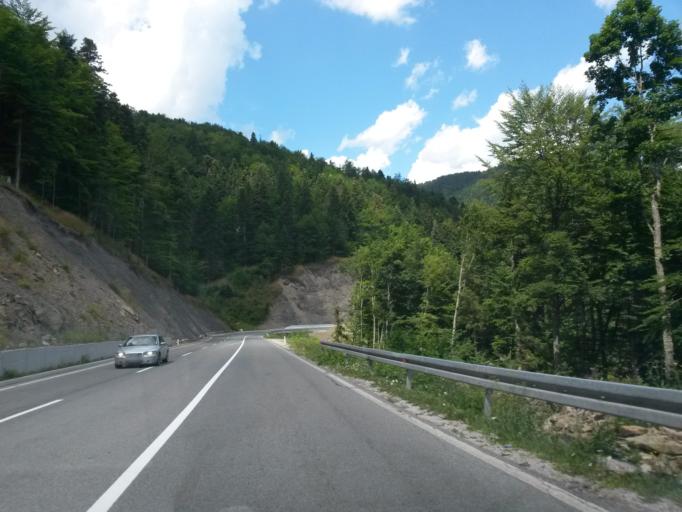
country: BA
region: Federation of Bosnia and Herzegovina
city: Bugojno
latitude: 44.0279
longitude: 17.3487
